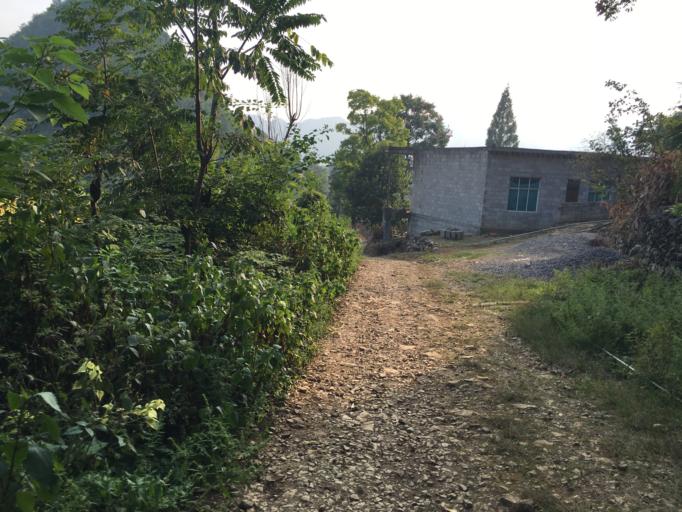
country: CN
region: Guangxi Zhuangzu Zizhiqu
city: Xinzhou
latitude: 25.4394
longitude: 105.6337
